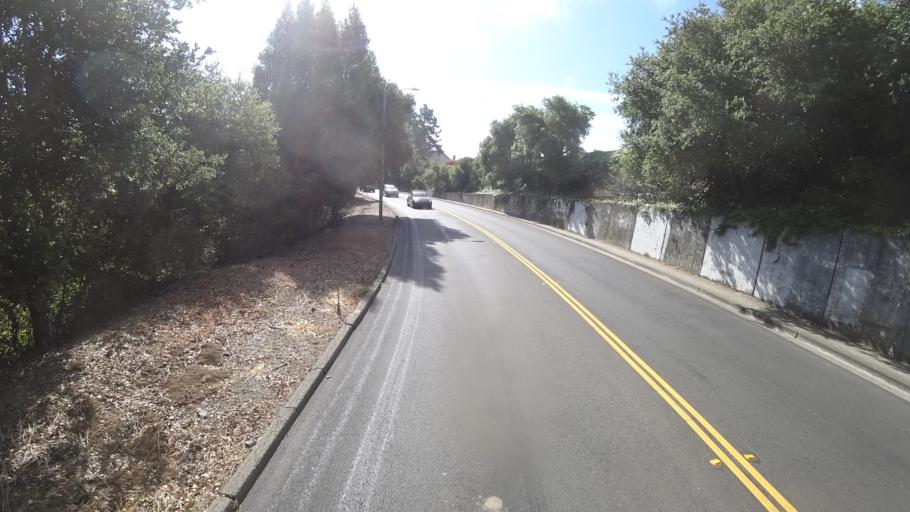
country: US
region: California
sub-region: Alameda County
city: Fairview
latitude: 37.6543
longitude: -122.0305
